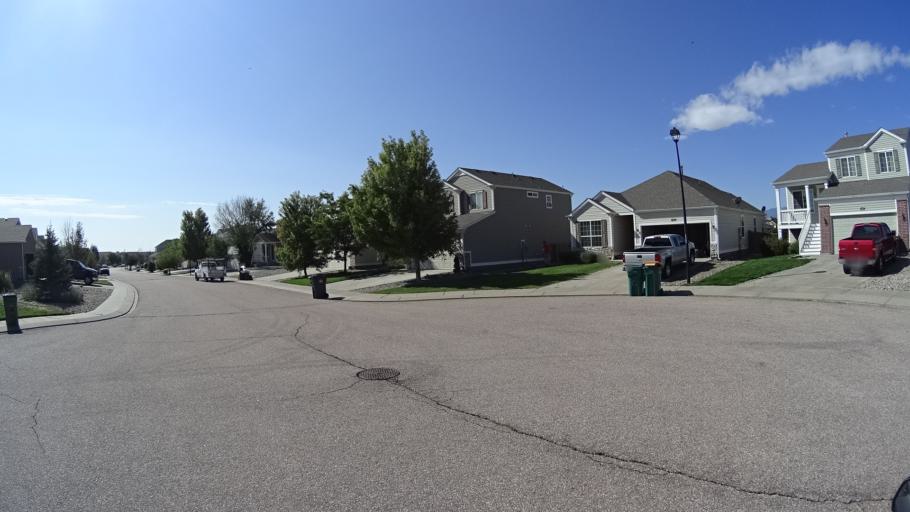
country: US
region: Colorado
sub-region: El Paso County
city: Cimarron Hills
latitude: 38.9295
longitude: -104.7004
